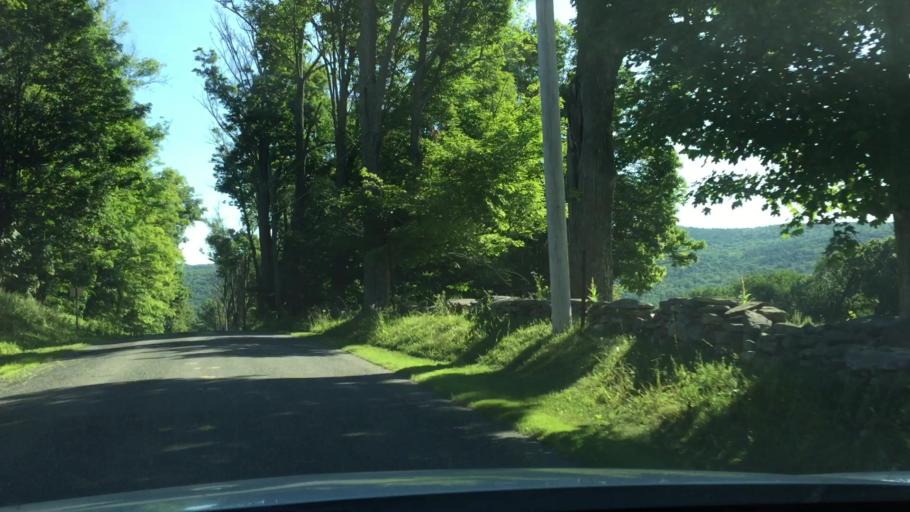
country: US
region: Massachusetts
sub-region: Berkshire County
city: Lee
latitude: 42.2358
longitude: -73.2111
